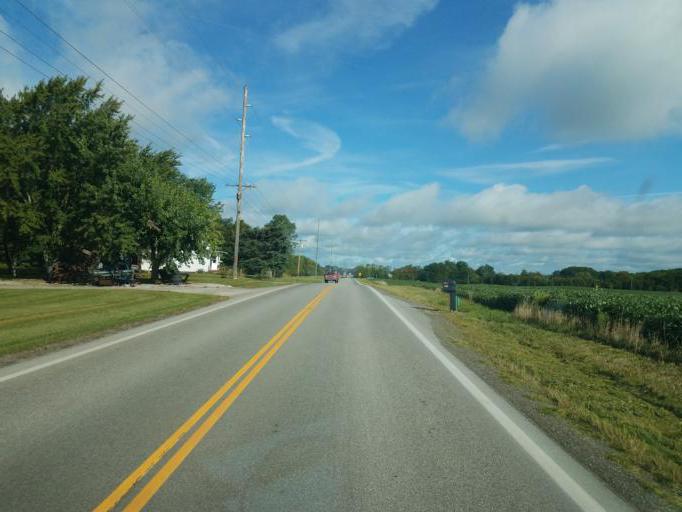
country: US
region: Ohio
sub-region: Wayne County
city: West Salem
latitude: 41.0022
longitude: -82.1145
